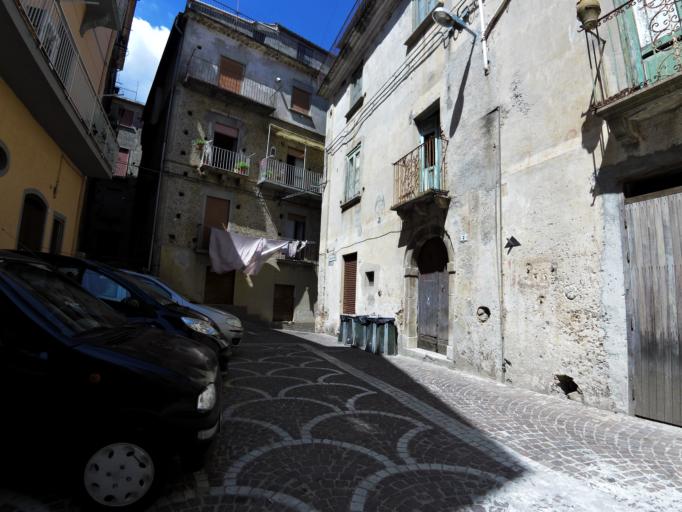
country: IT
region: Calabria
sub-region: Provincia di Reggio Calabria
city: Bivongi
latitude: 38.4822
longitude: 16.4529
